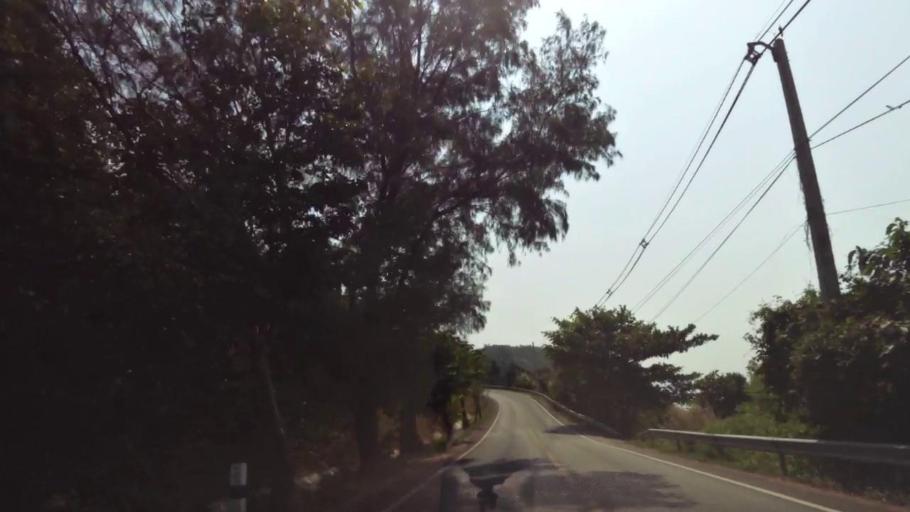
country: TH
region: Chanthaburi
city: Tha Mai
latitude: 12.5290
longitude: 101.9462
